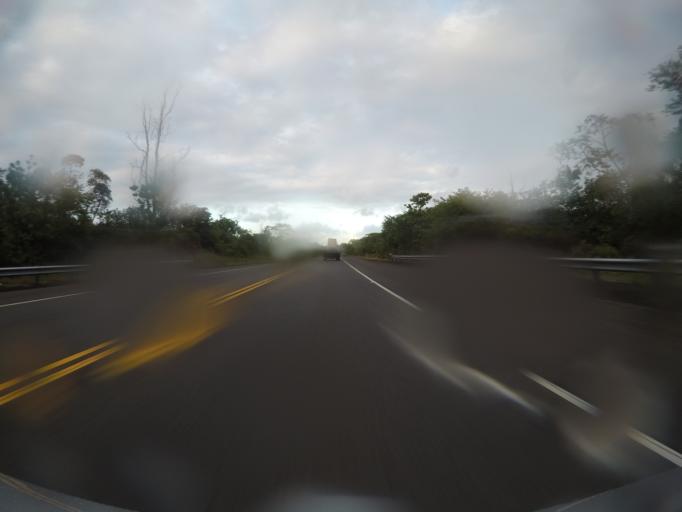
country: US
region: Hawaii
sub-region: Hawaii County
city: Hilo
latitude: 19.6938
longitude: -155.1000
